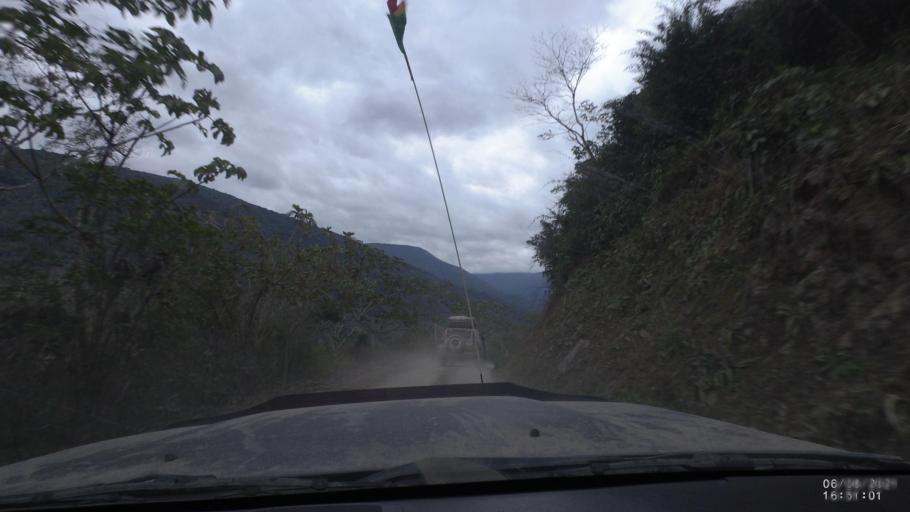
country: BO
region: La Paz
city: Quime
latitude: -16.4978
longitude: -66.7741
